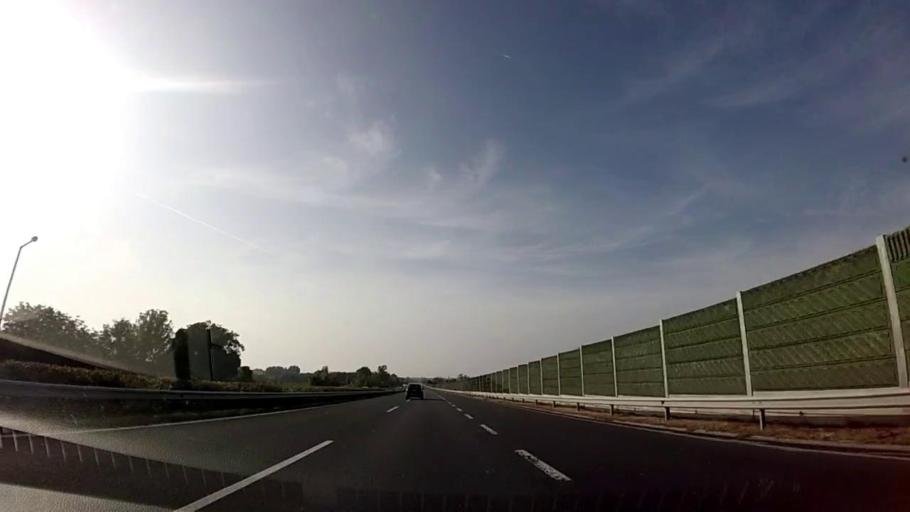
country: HU
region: Somogy
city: Balatonszabadi
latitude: 46.9535
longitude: 18.1531
